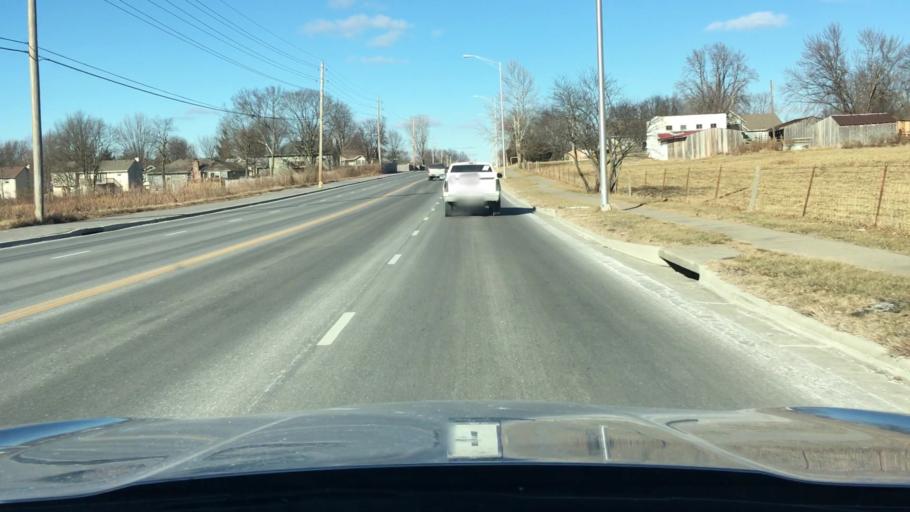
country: US
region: Missouri
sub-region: Jackson County
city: Lees Summit
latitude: 38.8990
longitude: -94.3959
